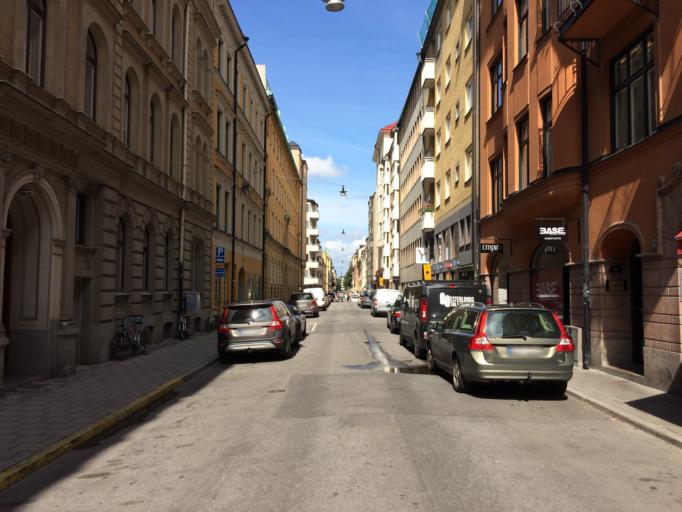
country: SE
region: Stockholm
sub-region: Stockholms Kommun
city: OEstermalm
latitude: 59.3361
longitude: 18.0811
